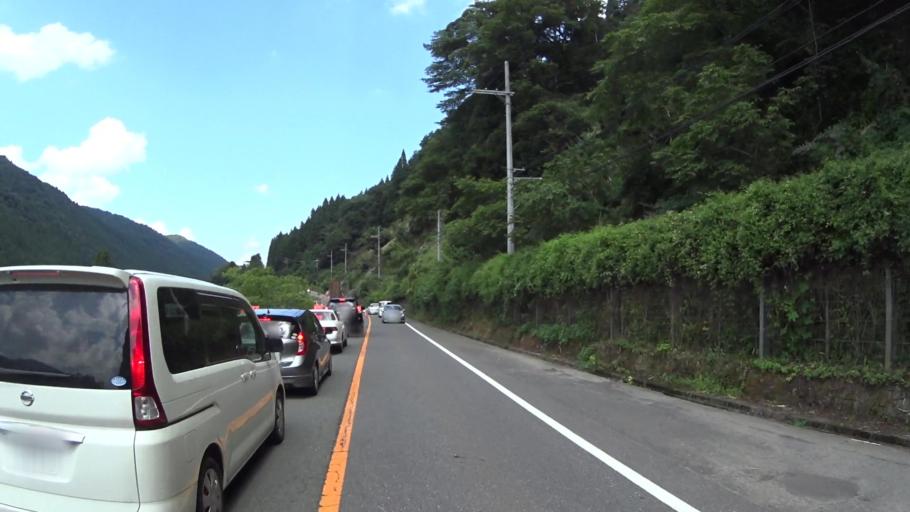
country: JP
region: Shiga Prefecture
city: Kitahama
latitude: 35.3135
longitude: 135.8956
